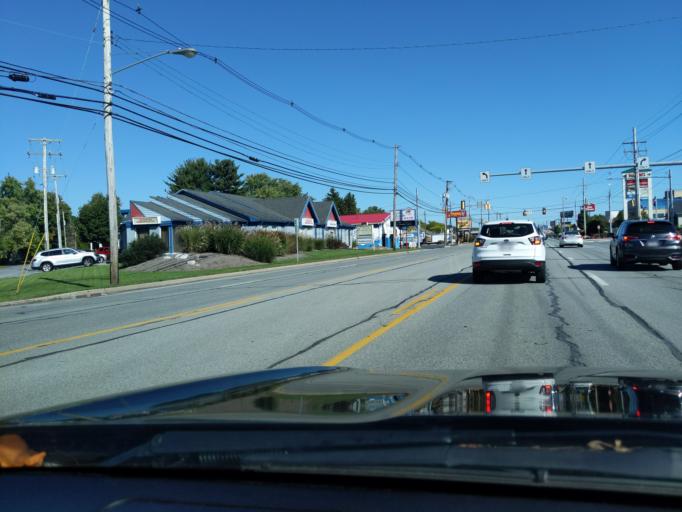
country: US
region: Pennsylvania
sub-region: Blair County
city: Lakemont
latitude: 40.4738
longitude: -78.4056
